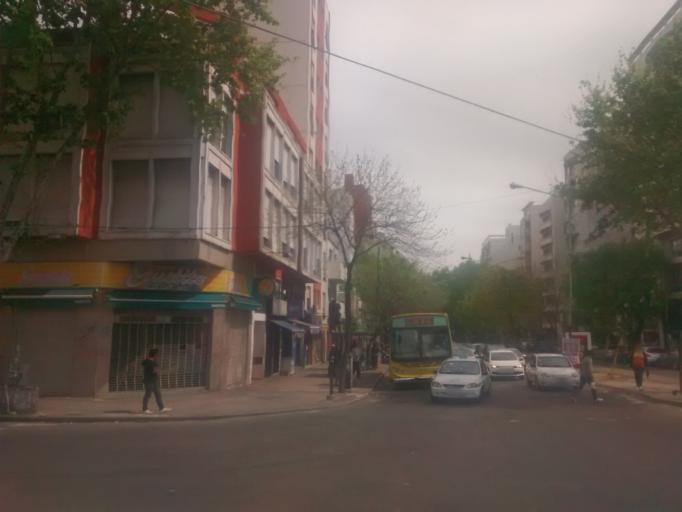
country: AR
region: Buenos Aires
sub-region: Partido de La Plata
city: La Plata
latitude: -34.9154
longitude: -57.9353
